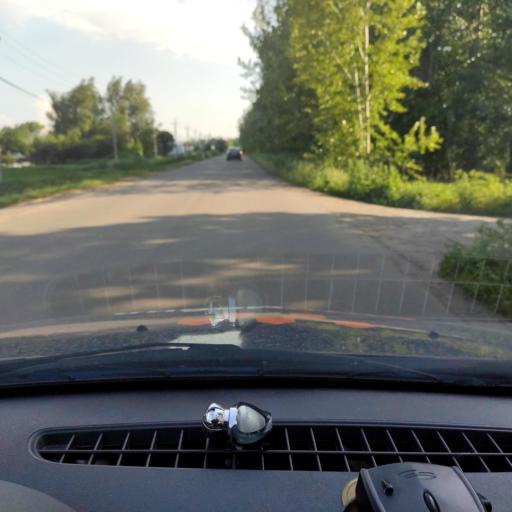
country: RU
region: Voronezj
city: Podkletnoye
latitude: 51.6040
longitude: 39.4296
